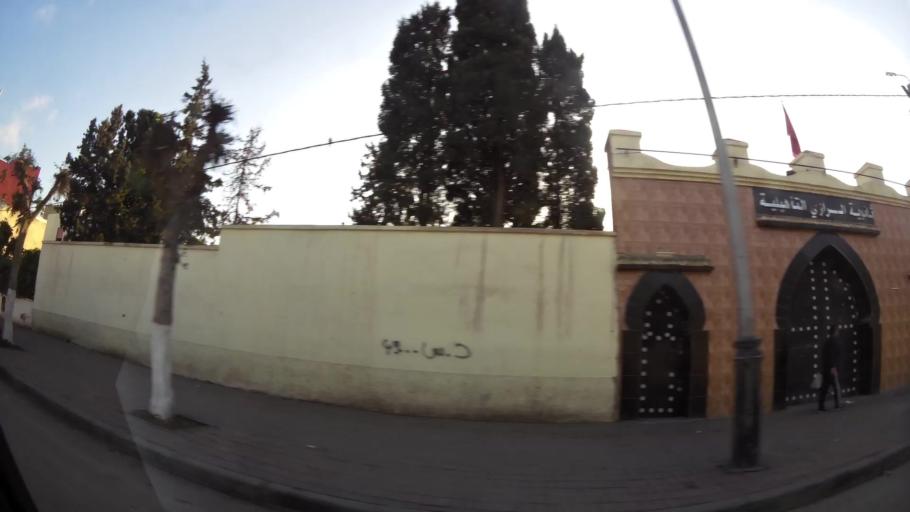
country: MA
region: Chaouia-Ouardigha
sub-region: Settat Province
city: Settat
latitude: 33.0049
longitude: -7.6161
